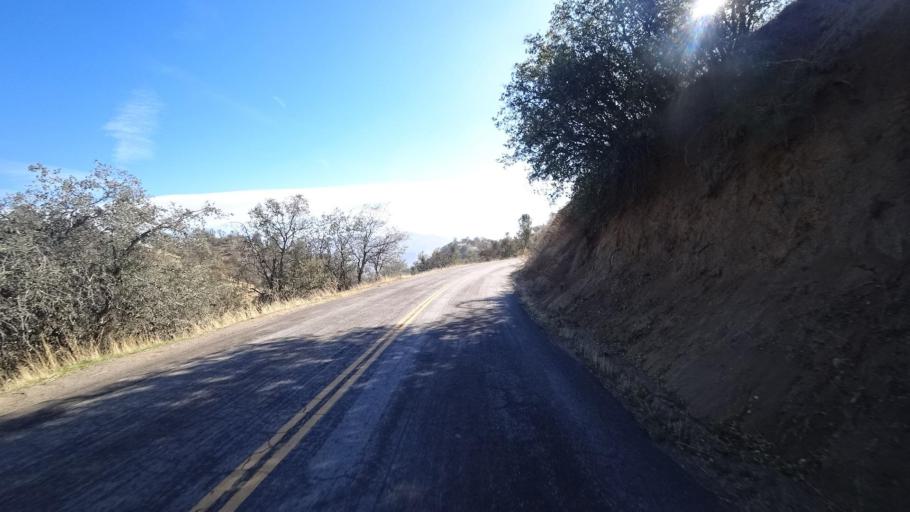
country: US
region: California
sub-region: Kern County
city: Bear Valley Springs
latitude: 35.3486
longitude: -118.5723
